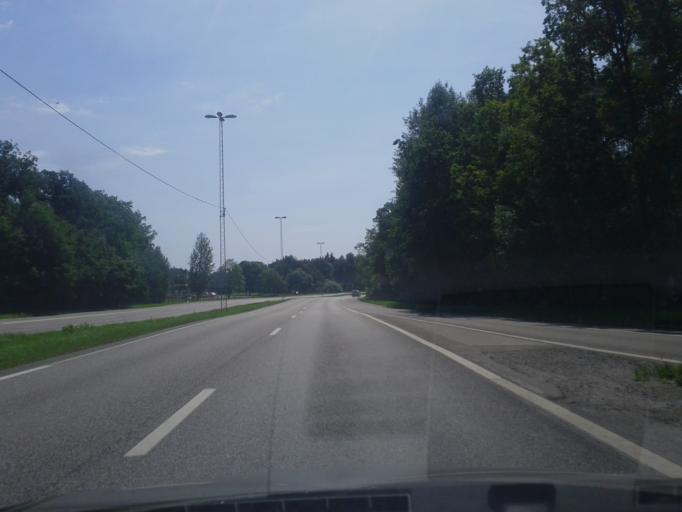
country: SE
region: Stockholm
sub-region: Huddinge Kommun
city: Huddinge
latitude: 59.2589
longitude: 18.0122
